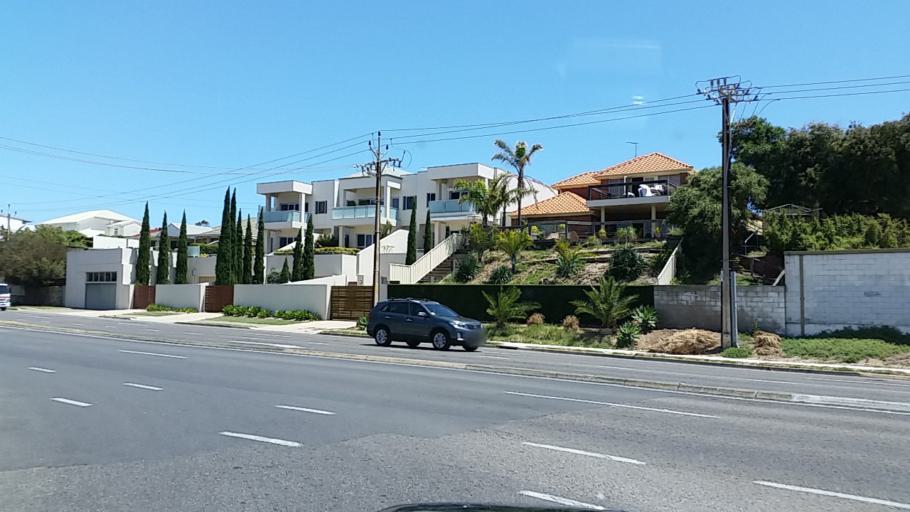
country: AU
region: South Australia
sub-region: Charles Sturt
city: Grange
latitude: -34.8946
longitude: 138.4889
